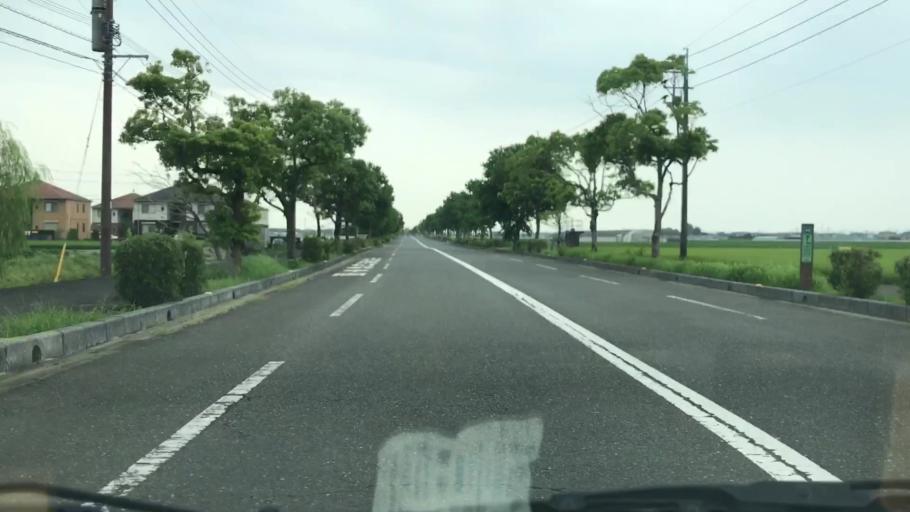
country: JP
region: Saga Prefecture
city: Saga-shi
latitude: 33.2077
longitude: 130.3037
